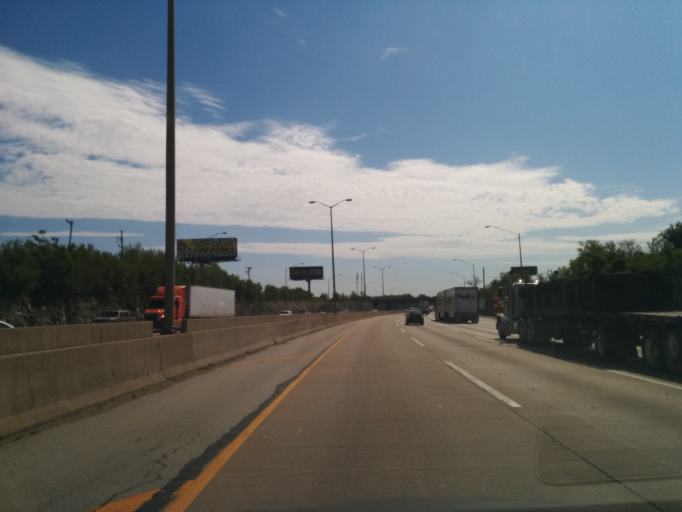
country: US
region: Illinois
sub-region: Cook County
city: East Hazel Crest
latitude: 41.5791
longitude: -87.6287
